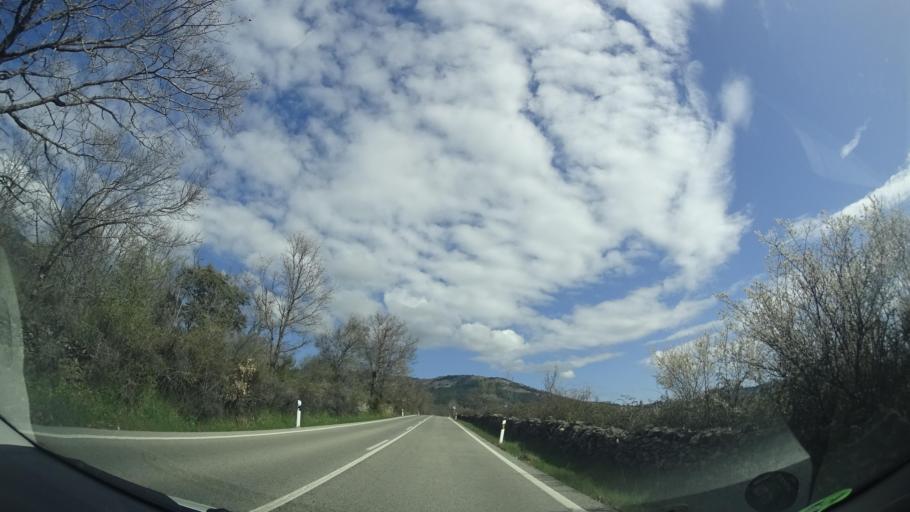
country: ES
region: Madrid
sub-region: Provincia de Madrid
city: Miraflores de la Sierra
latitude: 40.7976
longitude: -3.7749
